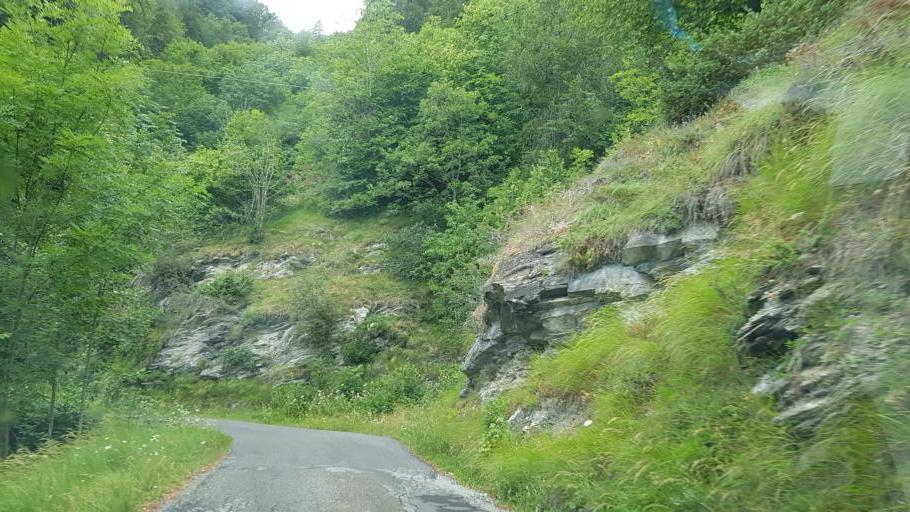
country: IT
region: Piedmont
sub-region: Provincia di Cuneo
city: Stroppo
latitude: 44.5163
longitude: 7.1146
